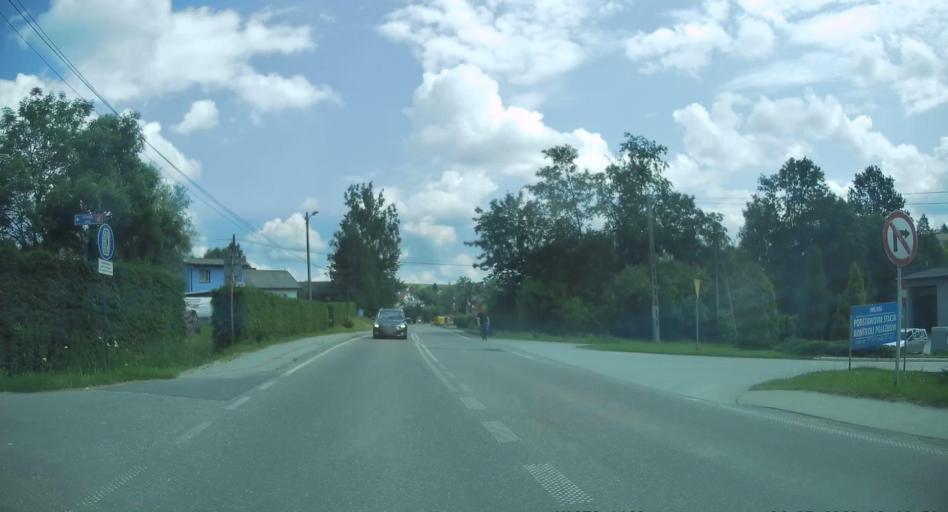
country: PL
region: Lesser Poland Voivodeship
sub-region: Powiat nowosadecki
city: Korzenna
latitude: 49.6721
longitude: 20.7768
